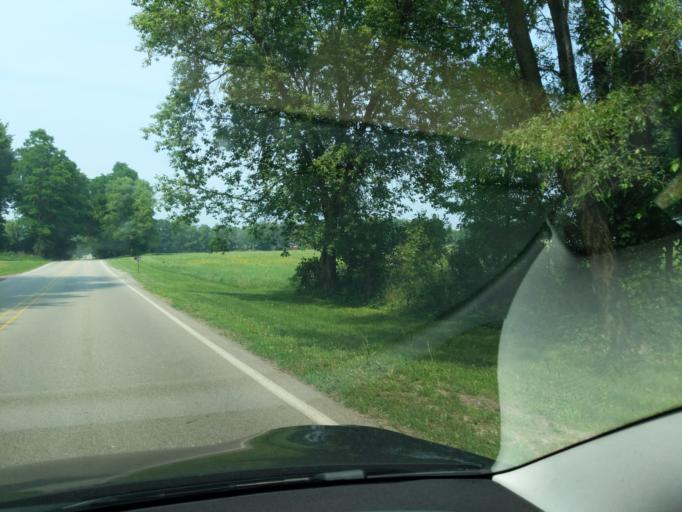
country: US
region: Michigan
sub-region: Clinton County
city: DeWitt
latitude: 42.8032
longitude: -84.5724
